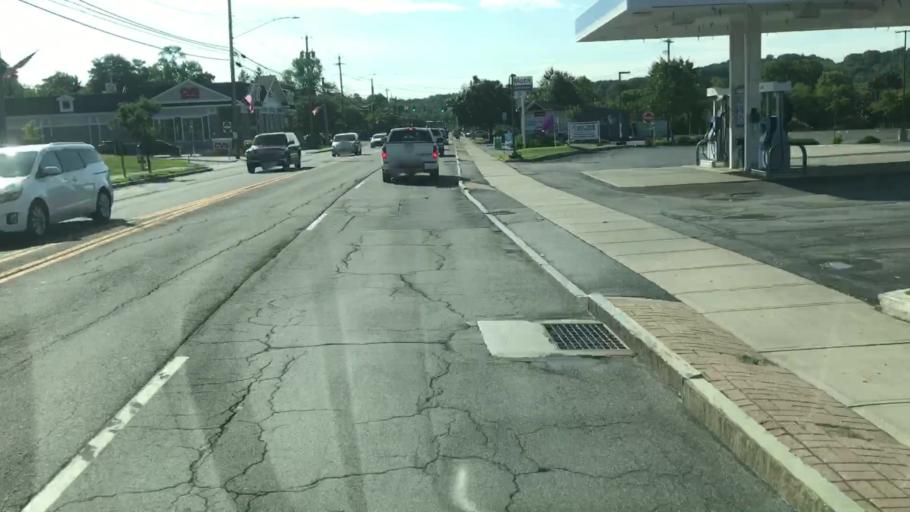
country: US
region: New York
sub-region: Onondaga County
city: Manlius
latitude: 43.0054
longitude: -75.9838
